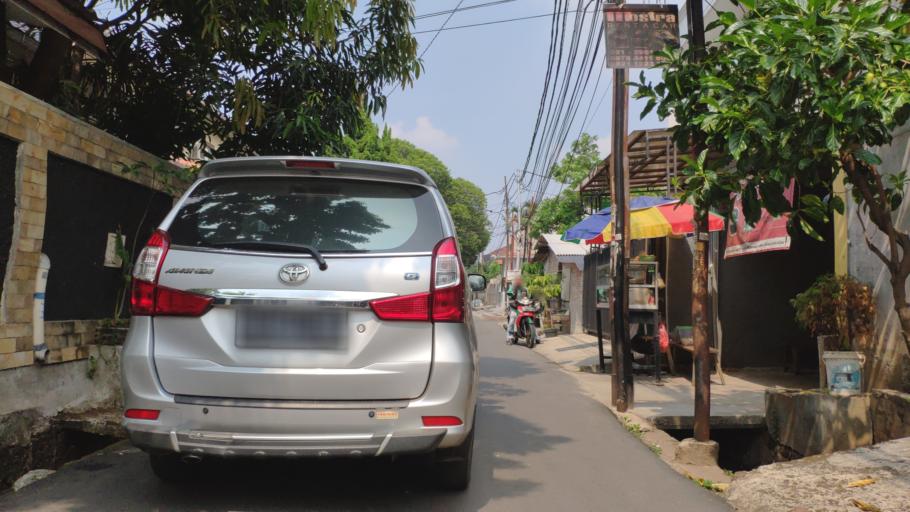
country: ID
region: Banten
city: South Tangerang
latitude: -6.2713
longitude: 106.7747
